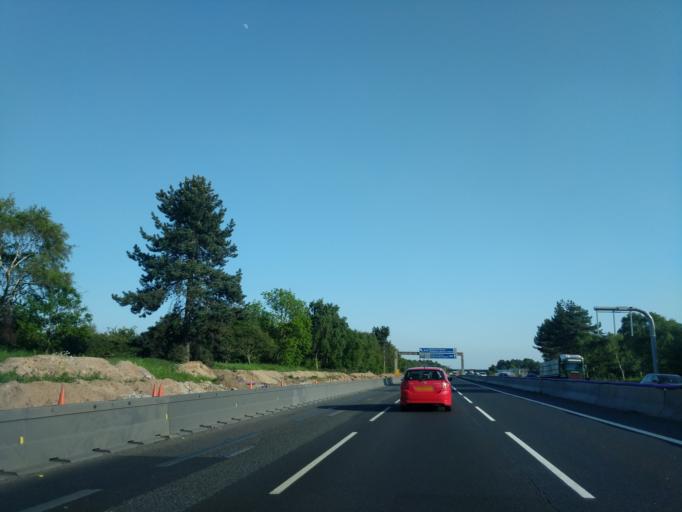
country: GB
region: England
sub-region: Cheshire East
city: Holmes Chapel
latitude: 53.2224
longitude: -2.3917
